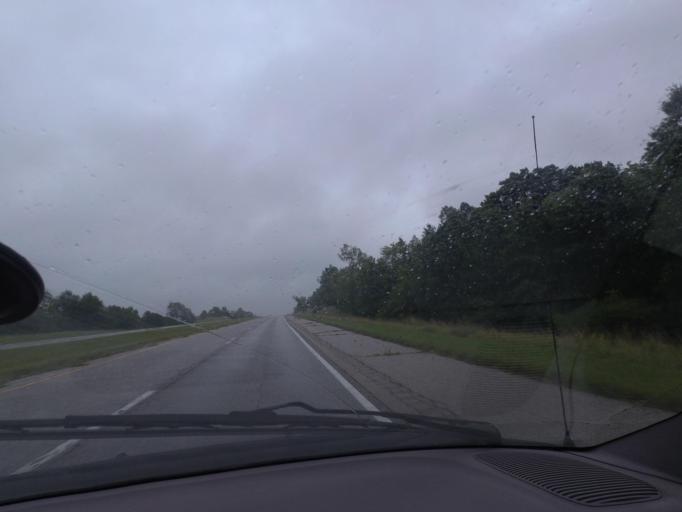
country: US
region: Illinois
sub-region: Pike County
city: Pittsfield
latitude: 39.6845
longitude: -90.8788
